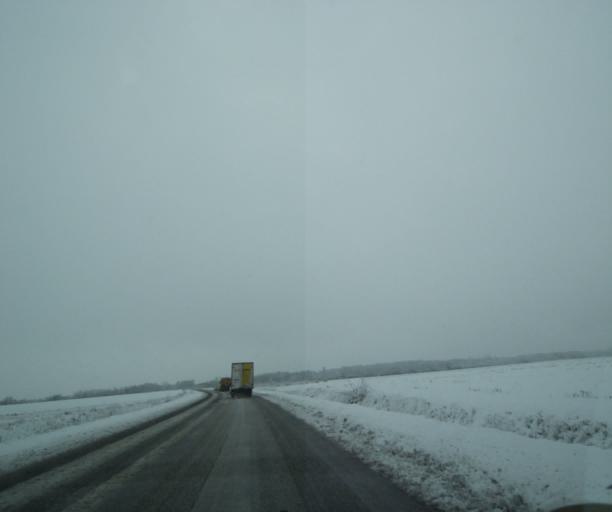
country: FR
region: Champagne-Ardenne
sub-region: Departement de la Haute-Marne
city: Saint-Dizier
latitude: 48.5939
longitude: 4.8916
